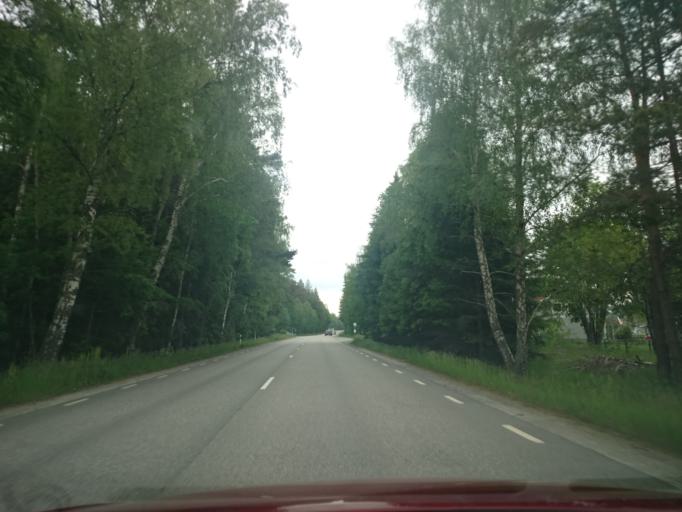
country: SE
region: Vaestra Goetaland
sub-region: Harryda Kommun
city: Hindas
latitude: 57.6970
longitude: 12.3604
